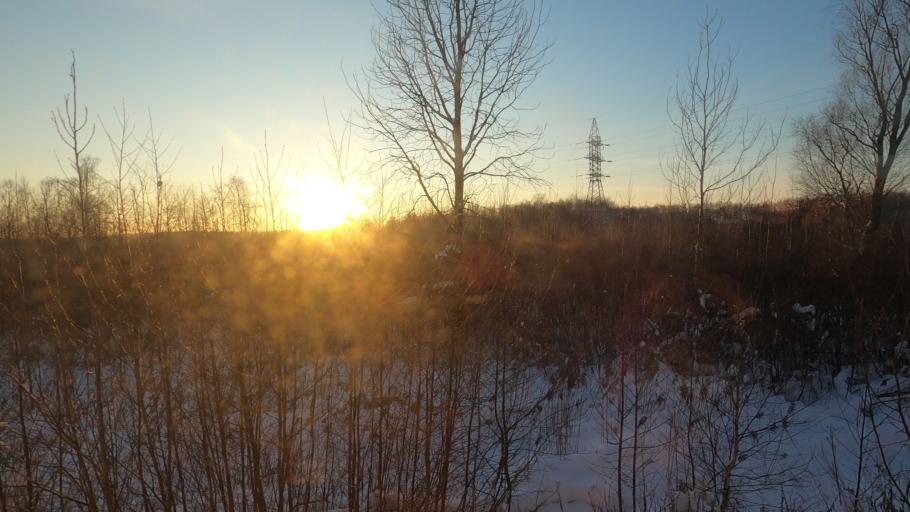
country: RU
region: Moskovskaya
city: Dmitrov
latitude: 56.3849
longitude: 37.5137
